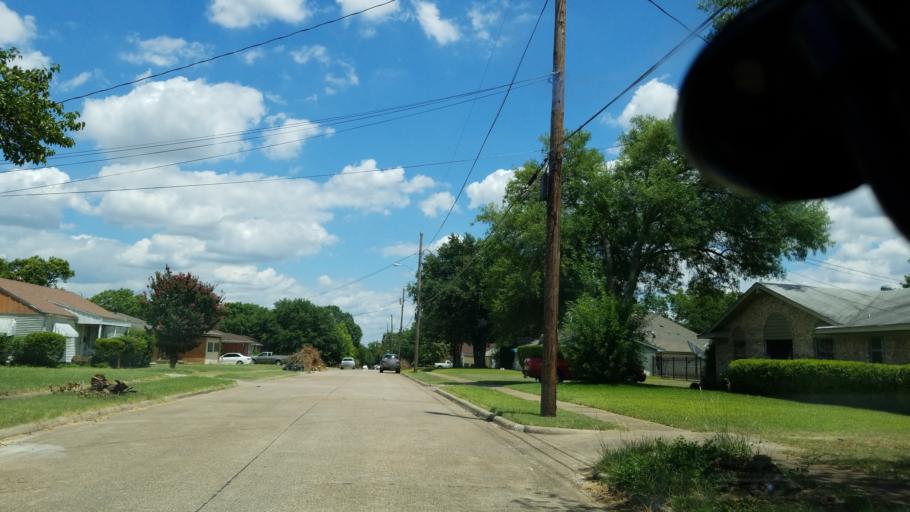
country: US
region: Texas
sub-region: Dallas County
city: Cockrell Hill
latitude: 32.6970
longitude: -96.8712
